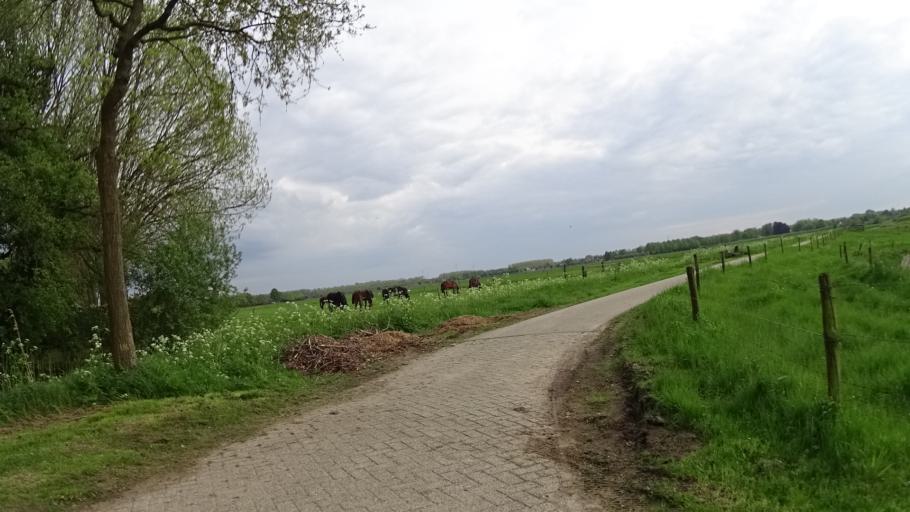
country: NL
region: North Brabant
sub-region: Gemeente Heusden
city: Heusden
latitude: 51.7324
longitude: 5.1485
